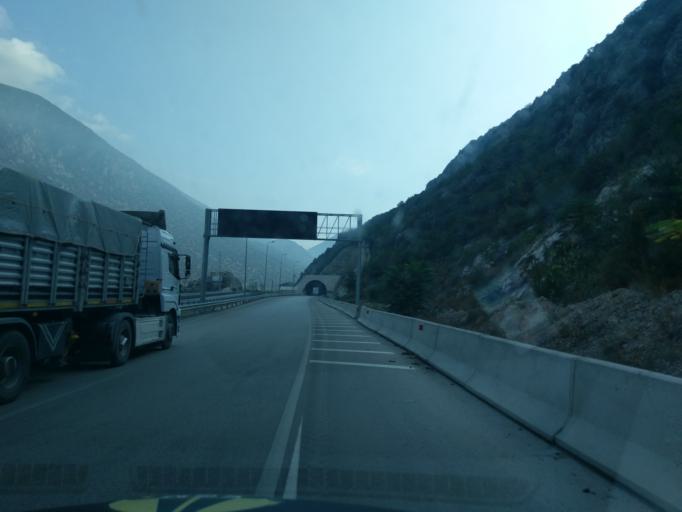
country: TR
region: Amasya
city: Akdag
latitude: 40.6938
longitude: 35.9299
